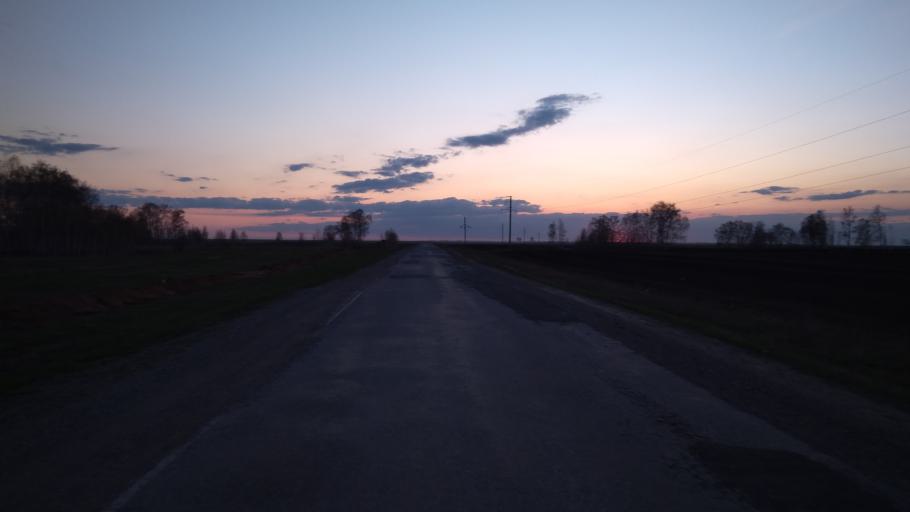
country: RU
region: Chelyabinsk
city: Bobrovka
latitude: 54.0858
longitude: 61.6688
